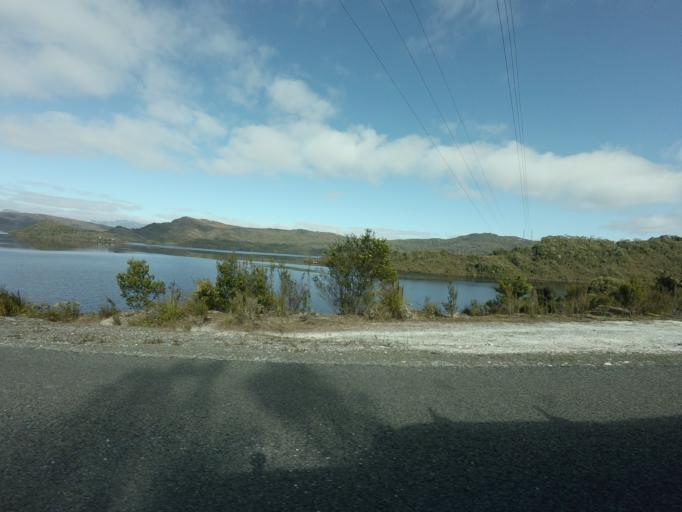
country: AU
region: Tasmania
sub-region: Huon Valley
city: Geeveston
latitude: -42.8287
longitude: 146.1262
